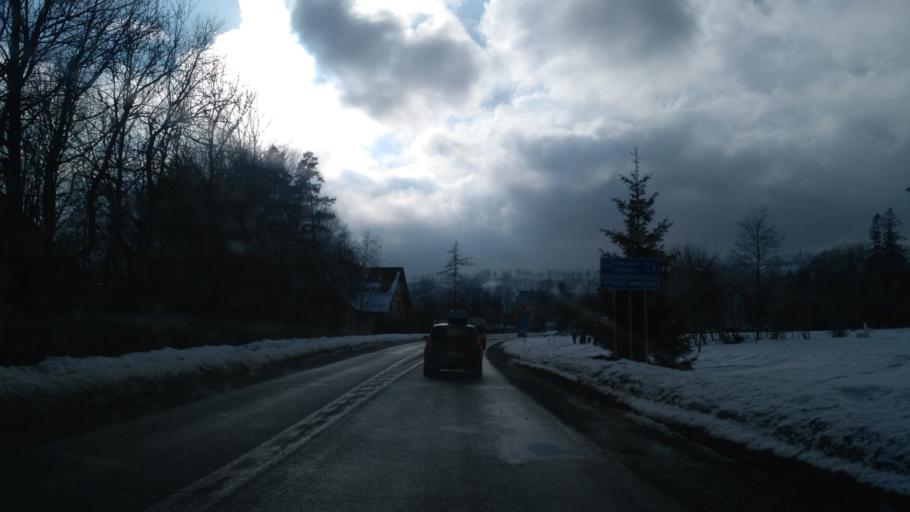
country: SK
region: Presovsky
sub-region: Okres Poprad
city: Nova Lesna
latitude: 49.1676
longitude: 20.2847
